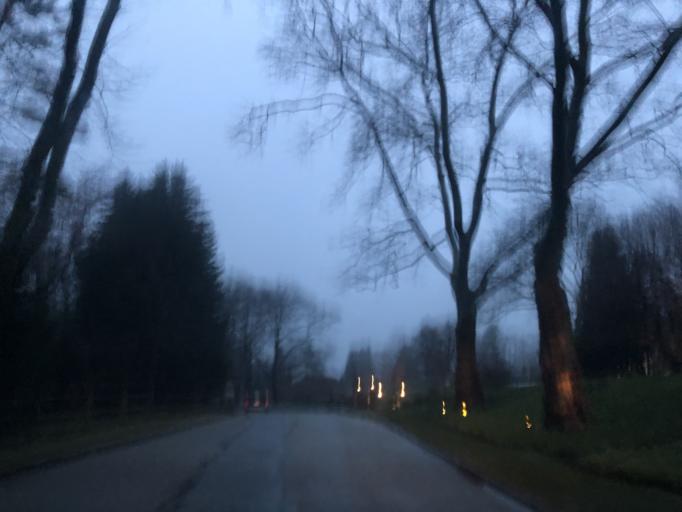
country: US
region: Pennsylvania
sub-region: Delaware County
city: Radnor
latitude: 40.0233
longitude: -75.3537
